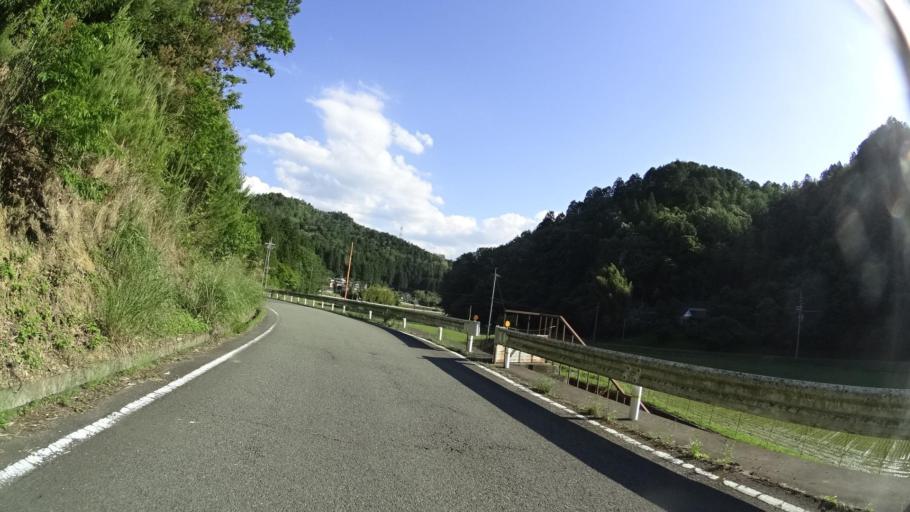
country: JP
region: Kyoto
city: Kameoka
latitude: 34.9687
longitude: 135.5625
